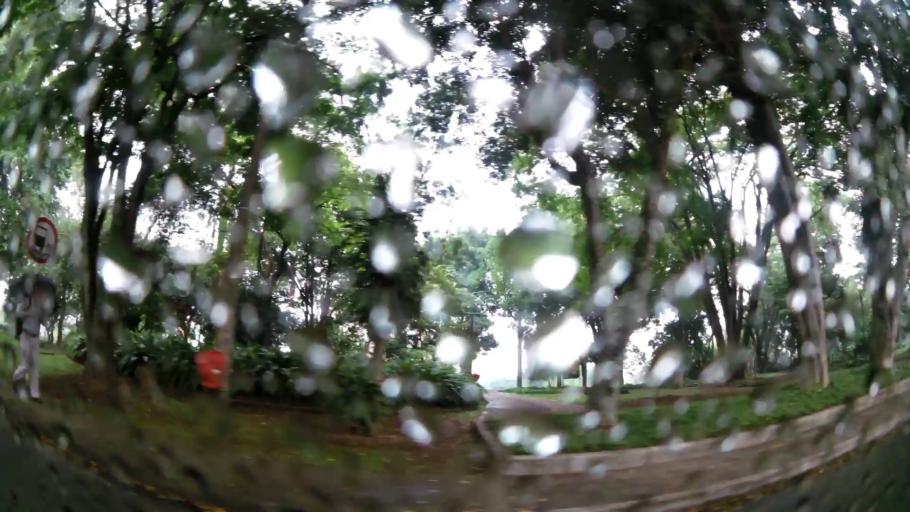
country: CO
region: Antioquia
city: Itagui
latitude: 6.2100
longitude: -75.5741
